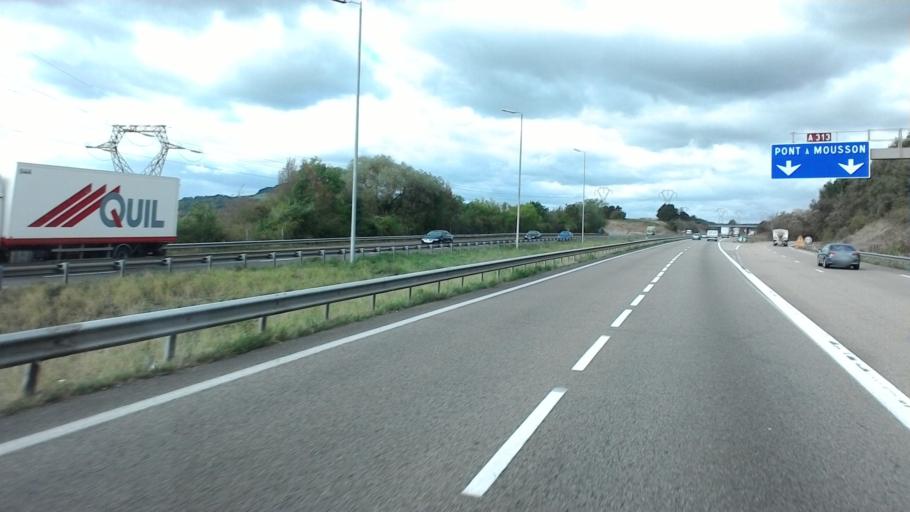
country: FR
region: Lorraine
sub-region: Departement de Meurthe-et-Moselle
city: Pont-a-Mousson
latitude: 48.8801
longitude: 6.0967
